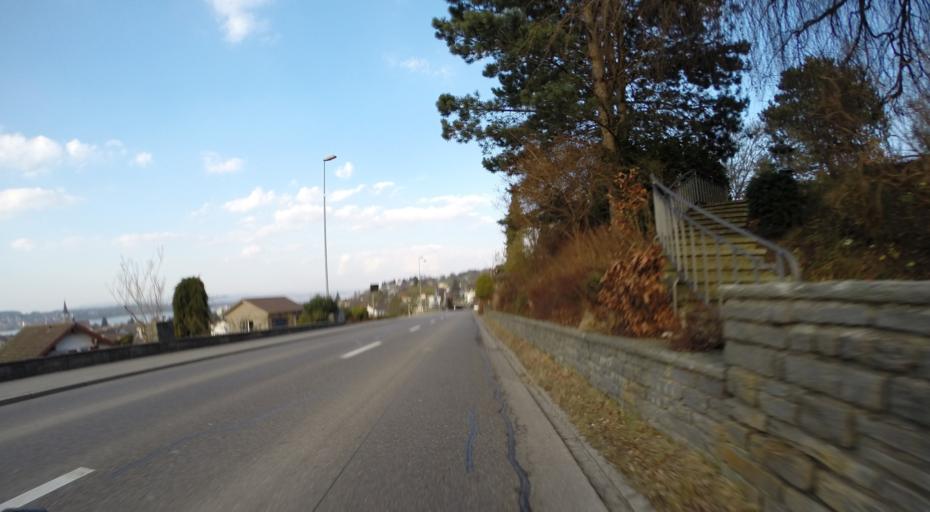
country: CH
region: Thurgau
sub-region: Frauenfeld District
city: Steckborn
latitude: 47.6616
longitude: 8.9833
